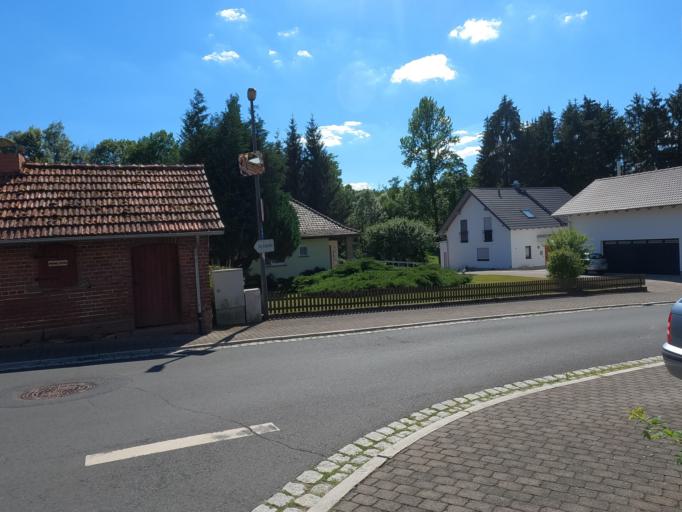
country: DE
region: Hesse
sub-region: Regierungsbezirk Darmstadt
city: Schluchtern
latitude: 50.3572
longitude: 9.5597
